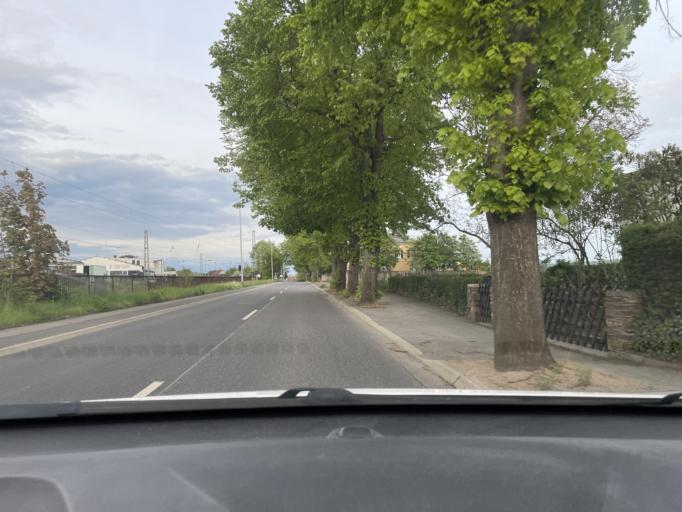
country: DE
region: Rheinland-Pfalz
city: Oestrich-Winkel
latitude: 49.9914
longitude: 7.9933
